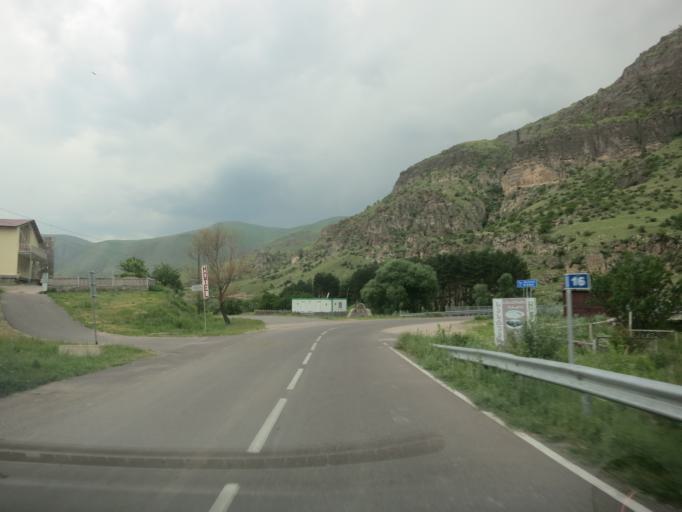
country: TR
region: Ardahan
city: Kurtkale
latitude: 41.3770
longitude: 43.2821
